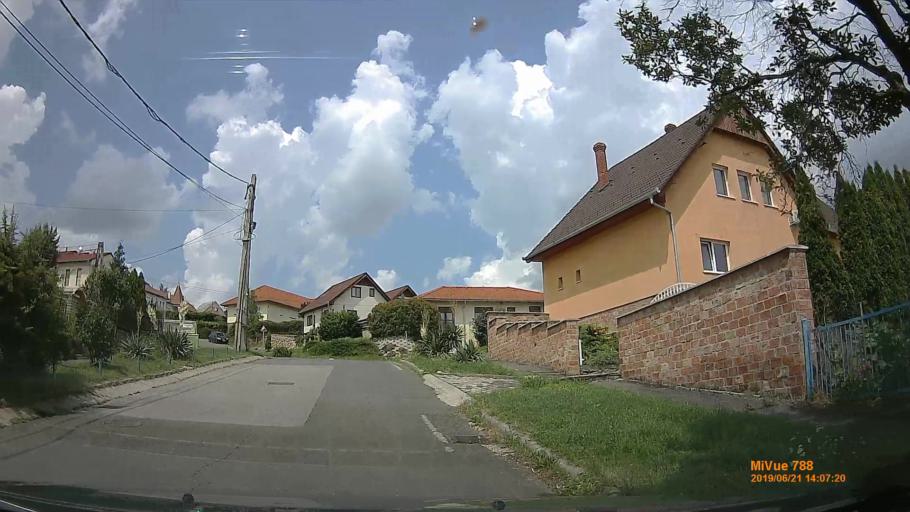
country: HU
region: Baranya
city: Pellerd
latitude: 46.0688
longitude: 18.1697
